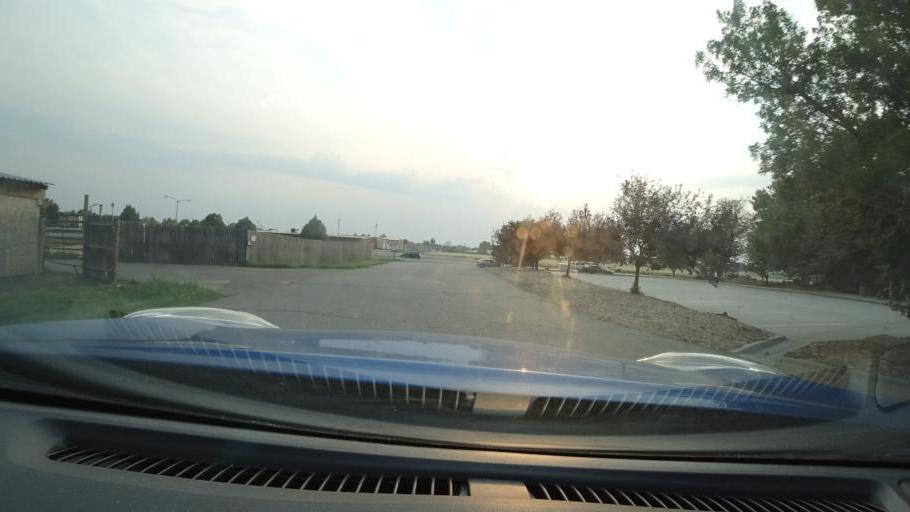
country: US
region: Colorado
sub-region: Adams County
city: Aurora
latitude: 39.7383
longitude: -104.7903
